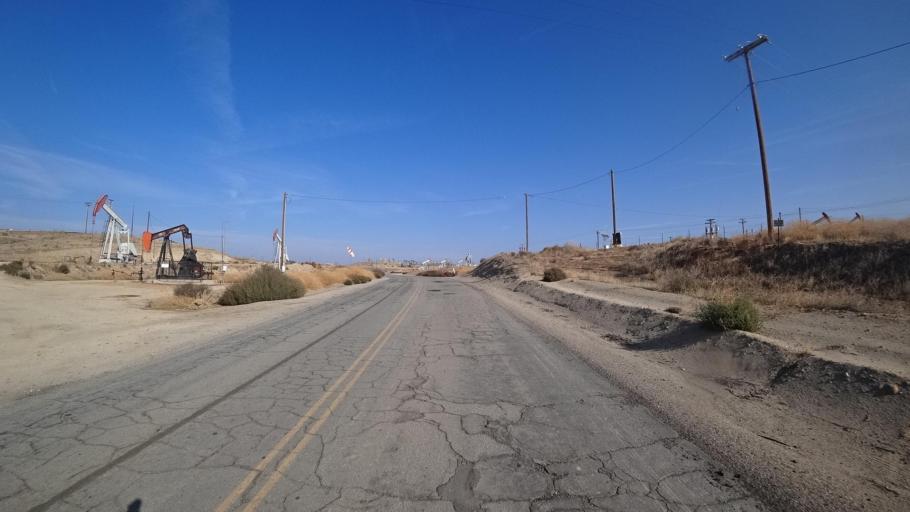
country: US
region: California
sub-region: Kern County
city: Oildale
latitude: 35.4736
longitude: -119.0463
